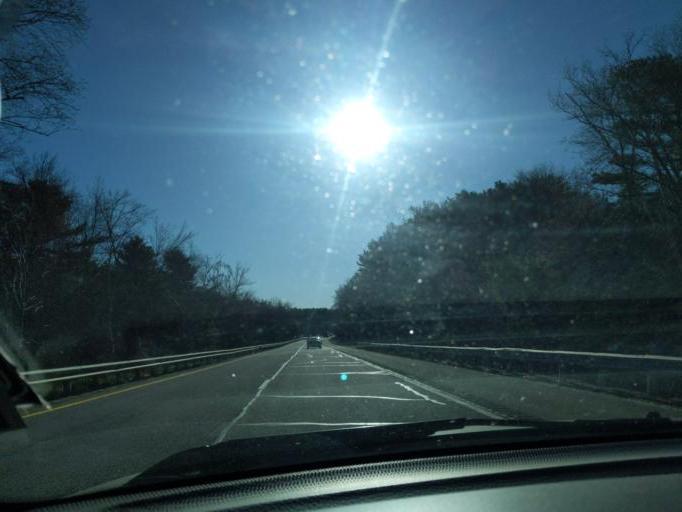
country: US
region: Massachusetts
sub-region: Essex County
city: Essex
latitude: 42.5912
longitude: -70.7816
